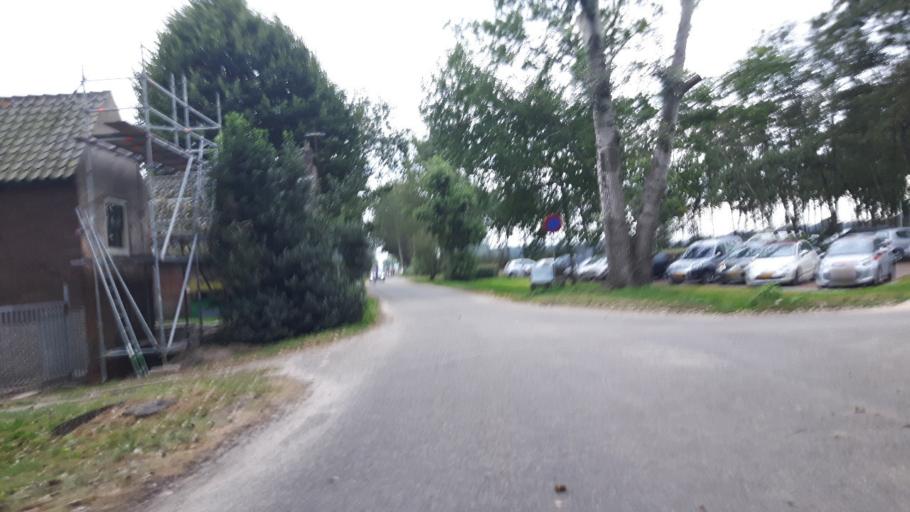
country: NL
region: North Holland
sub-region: Gemeente Bloemendaal
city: Bennebroek
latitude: 52.3202
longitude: 4.5671
